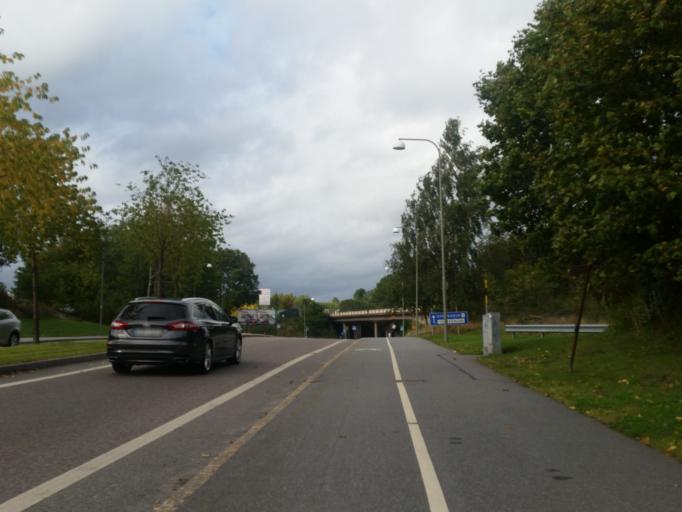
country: SE
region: Stockholm
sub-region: Stockholms Kommun
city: Arsta
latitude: 59.2465
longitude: 18.0906
